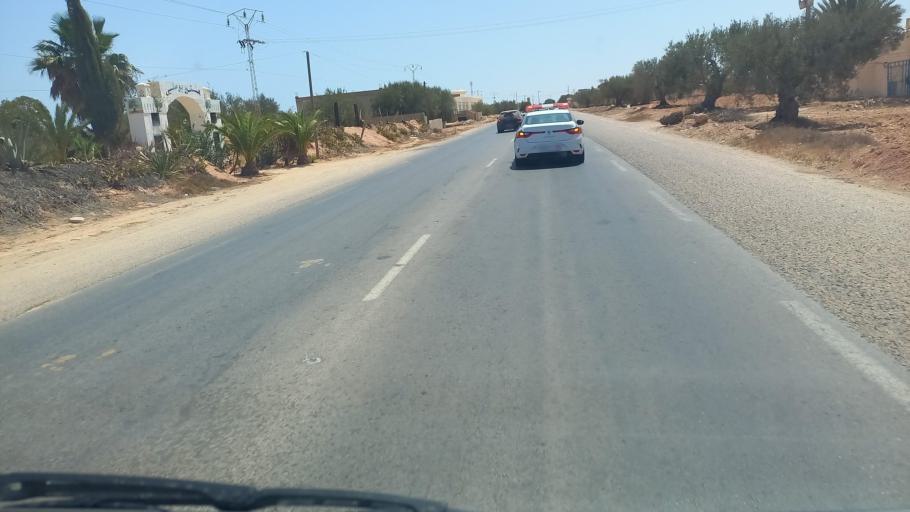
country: TN
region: Madanin
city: Zarzis
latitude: 33.5443
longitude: 11.0738
